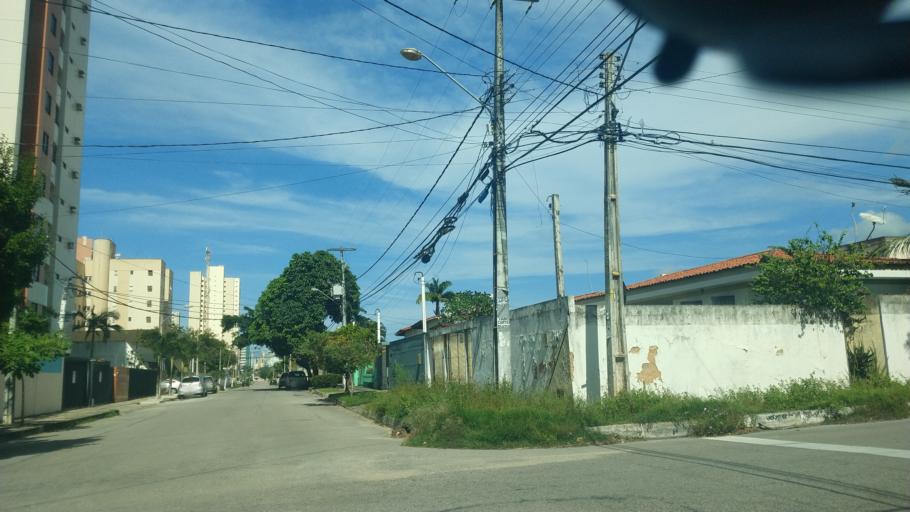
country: BR
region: Rio Grande do Norte
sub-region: Natal
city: Natal
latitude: -5.8624
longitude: -35.1968
